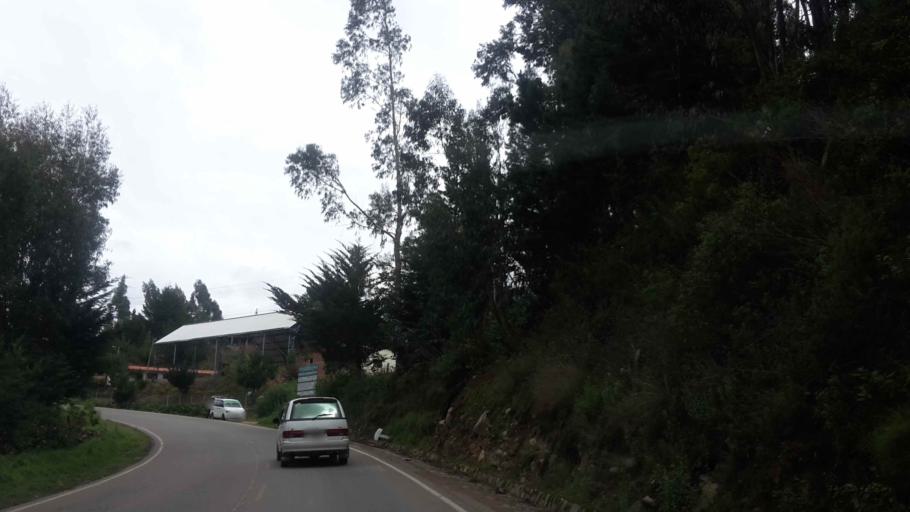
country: BO
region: Cochabamba
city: Totora
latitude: -17.5307
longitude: -65.3787
